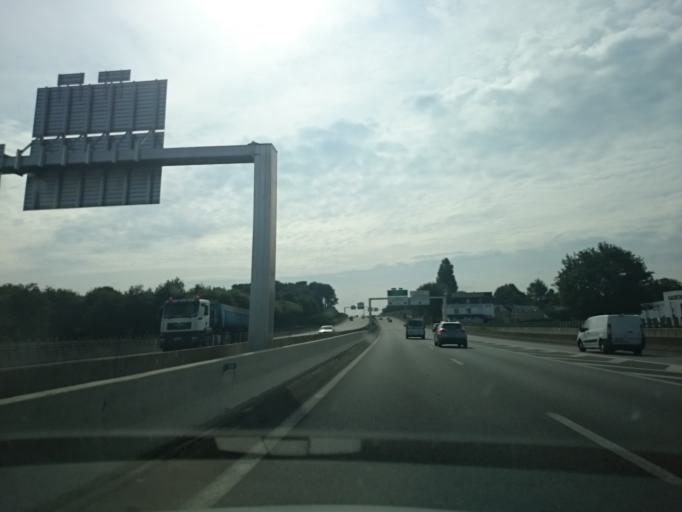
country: FR
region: Brittany
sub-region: Departement du Morbihan
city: Theix
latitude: 47.6443
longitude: -2.6963
